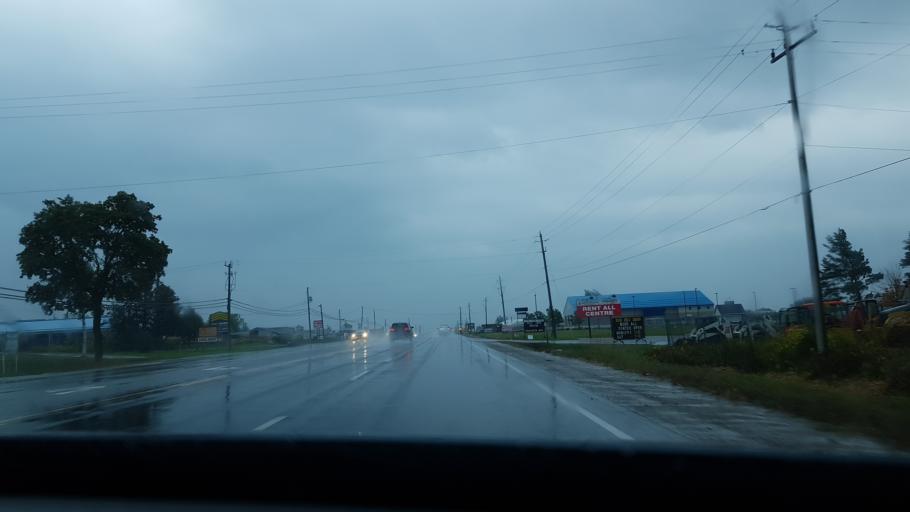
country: CA
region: Ontario
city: Peterborough
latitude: 44.3424
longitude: -78.3550
